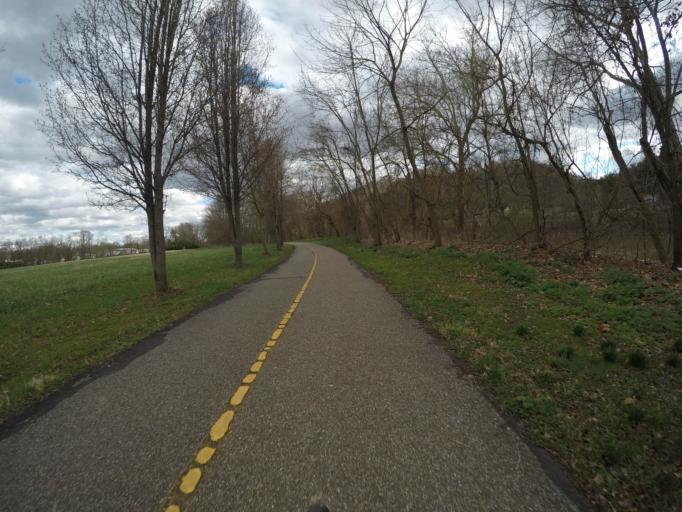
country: US
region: Ohio
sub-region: Washington County
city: Marietta
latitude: 39.4254
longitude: -81.4718
